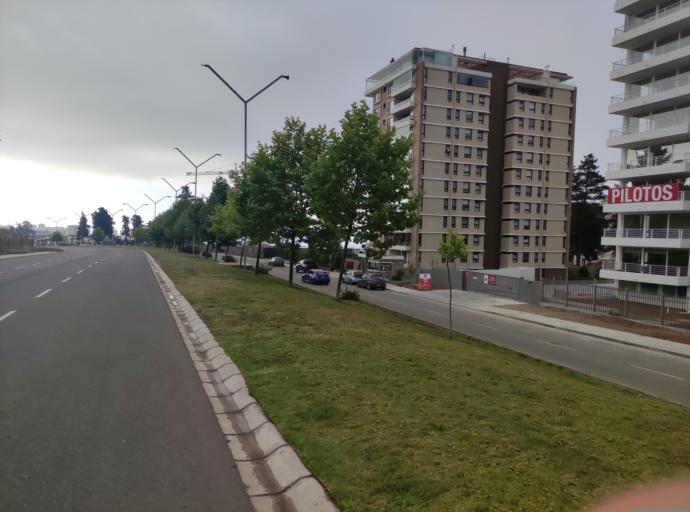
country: CL
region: Valparaiso
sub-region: Provincia de Valparaiso
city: Vina del Mar
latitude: -32.9435
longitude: -71.5184
